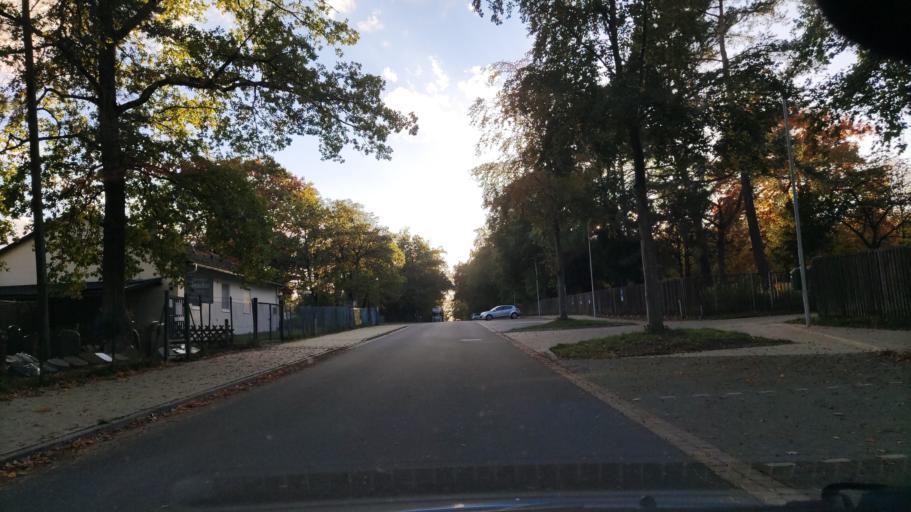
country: DE
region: Lower Saxony
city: Munster
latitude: 52.9801
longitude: 10.0822
